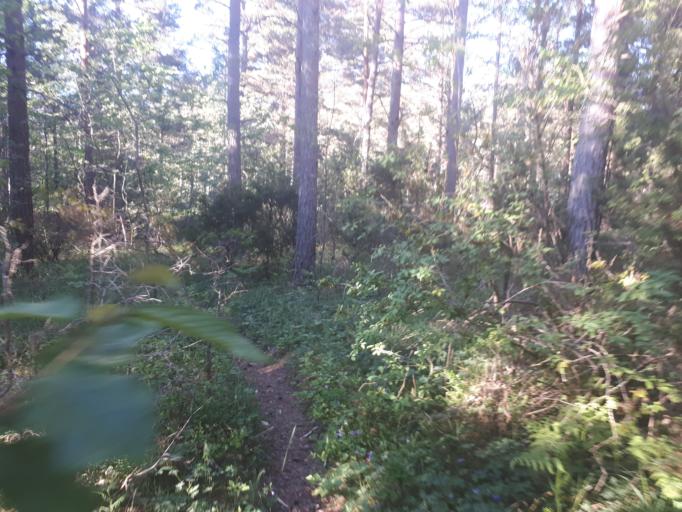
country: SE
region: Gotland
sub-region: Gotland
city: Visby
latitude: 57.6043
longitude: 18.2892
